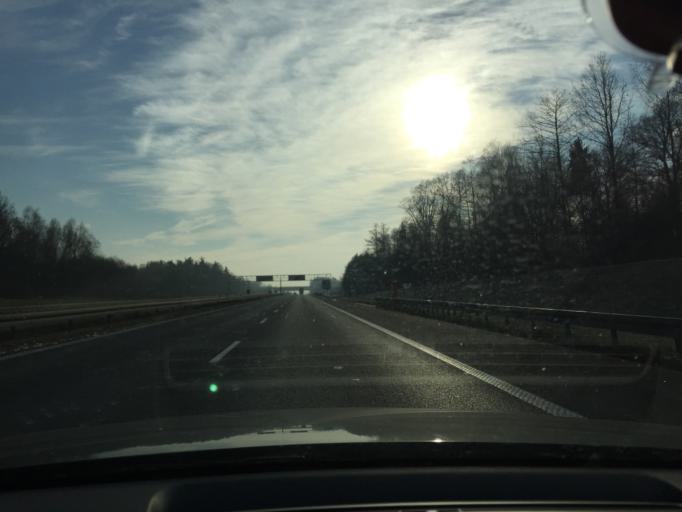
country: PL
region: Silesian Voivodeship
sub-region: Powiat gliwicki
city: Sosnicowice
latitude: 50.3363
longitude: 18.5445
